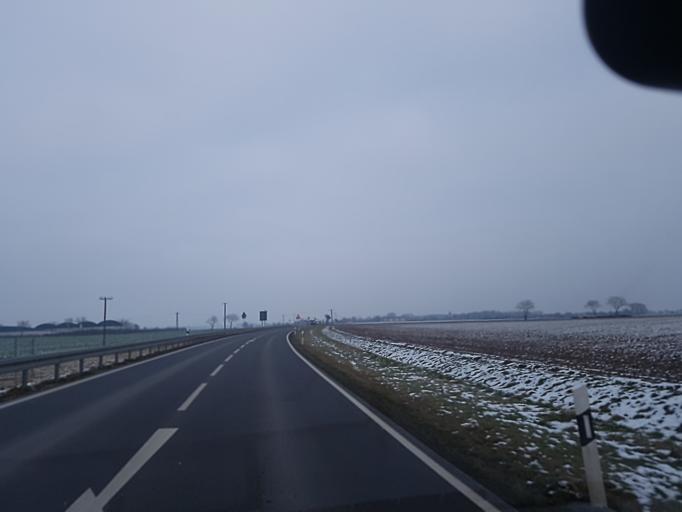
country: DE
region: Saxony
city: Naundorf
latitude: 51.2490
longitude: 13.0892
